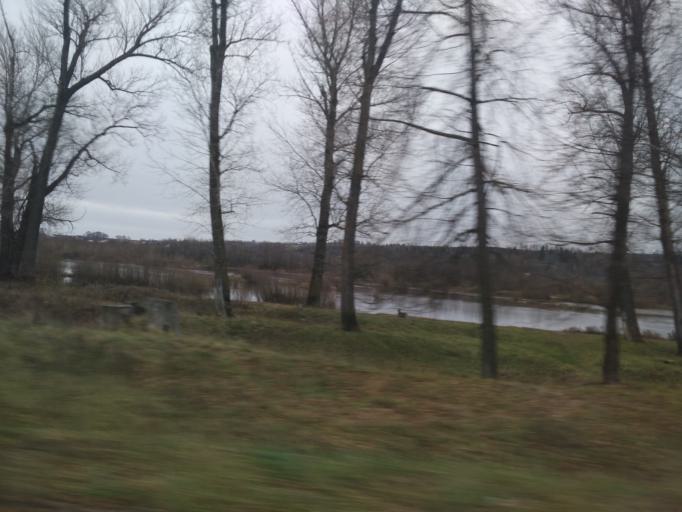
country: RU
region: Kirov
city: Krasnaya Polyana
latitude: 56.2458
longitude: 51.1979
